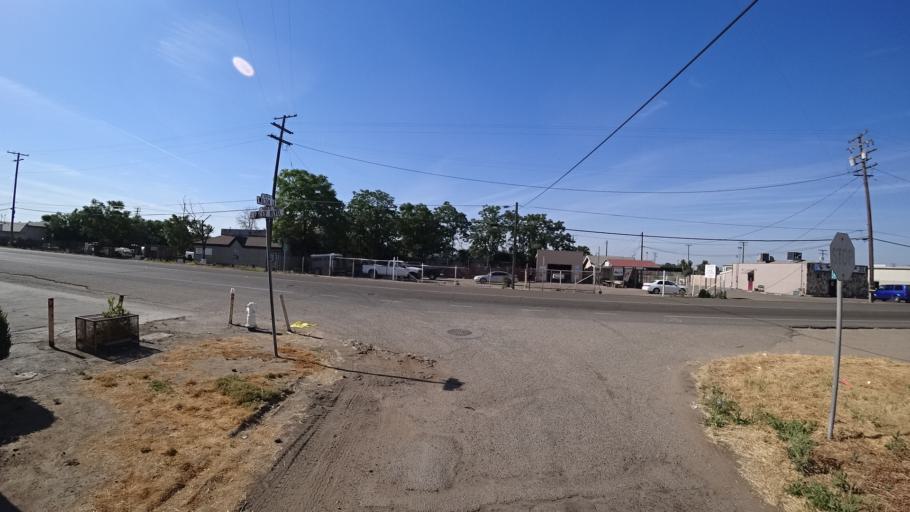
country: US
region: California
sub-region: Kings County
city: Hanford
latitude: 36.3282
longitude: -119.6326
